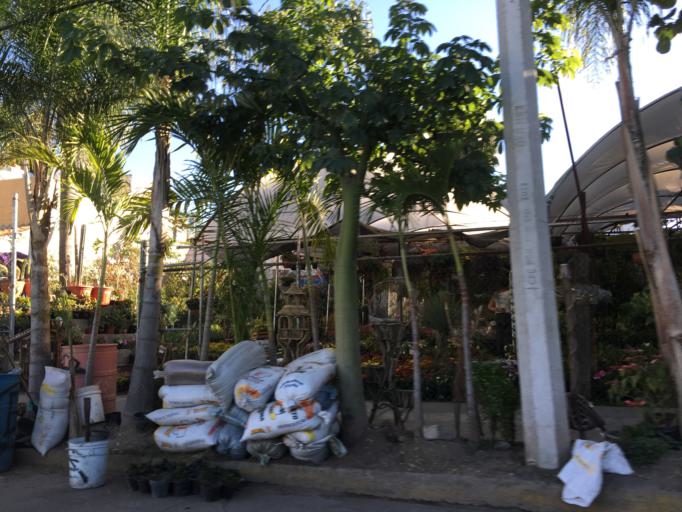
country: MX
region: Jalisco
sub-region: Zapopan
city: Zapopan
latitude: 20.7072
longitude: -103.3466
